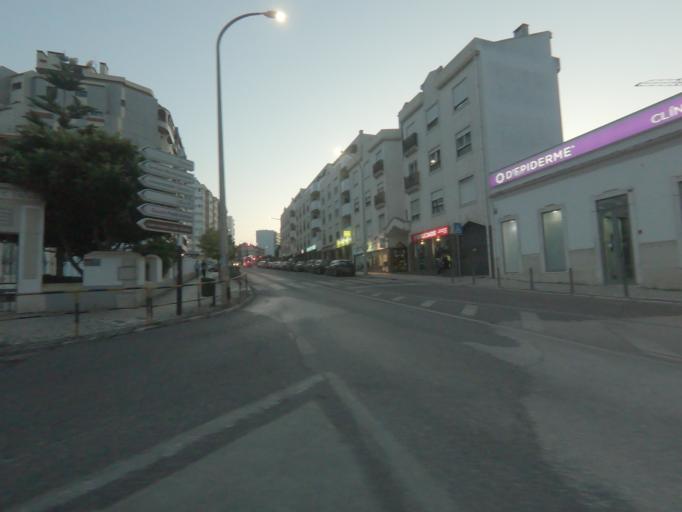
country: PT
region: Leiria
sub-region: Leiria
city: Leiria
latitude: 39.7404
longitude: -8.8032
